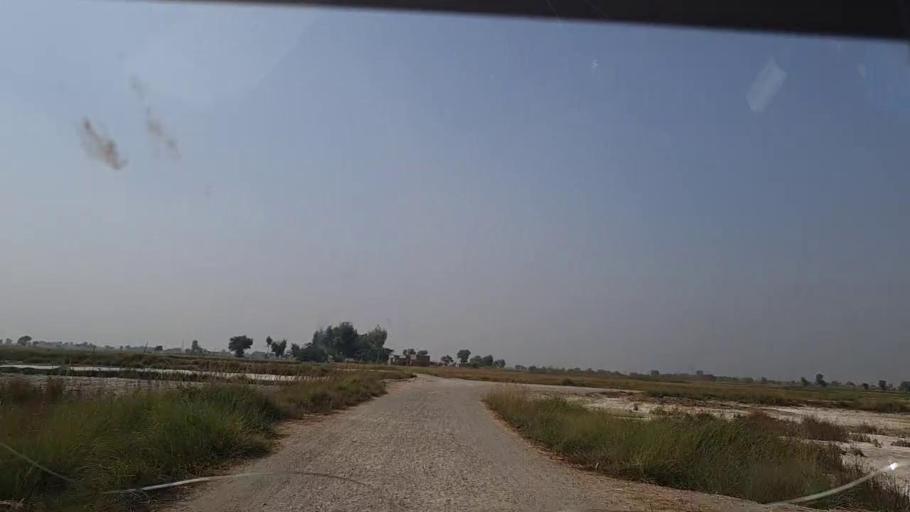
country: PK
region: Sindh
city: Shikarpur
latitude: 28.0913
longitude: 68.5999
